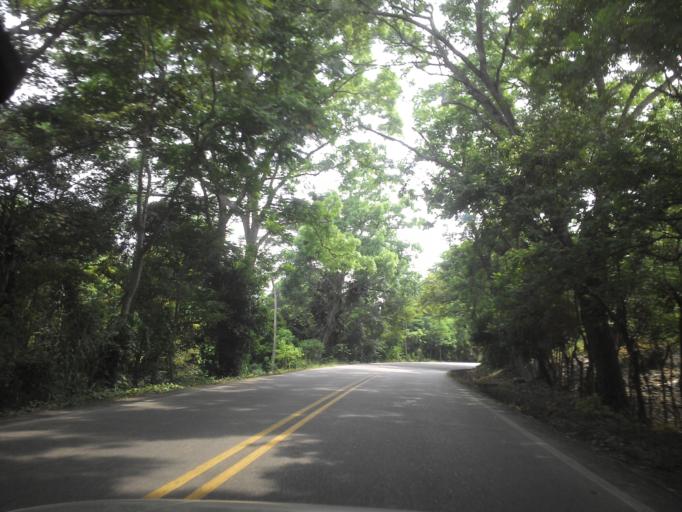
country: MX
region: Veracruz
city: Gutierrez Zamora
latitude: 20.4616
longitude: -97.1384
